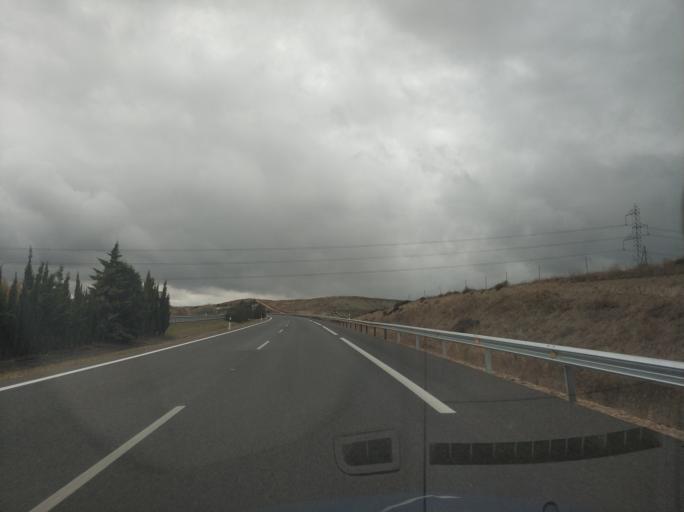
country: ES
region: Castille and Leon
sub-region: Provincia de Palencia
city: Soto de Cerrato
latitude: 41.9749
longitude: -4.4486
